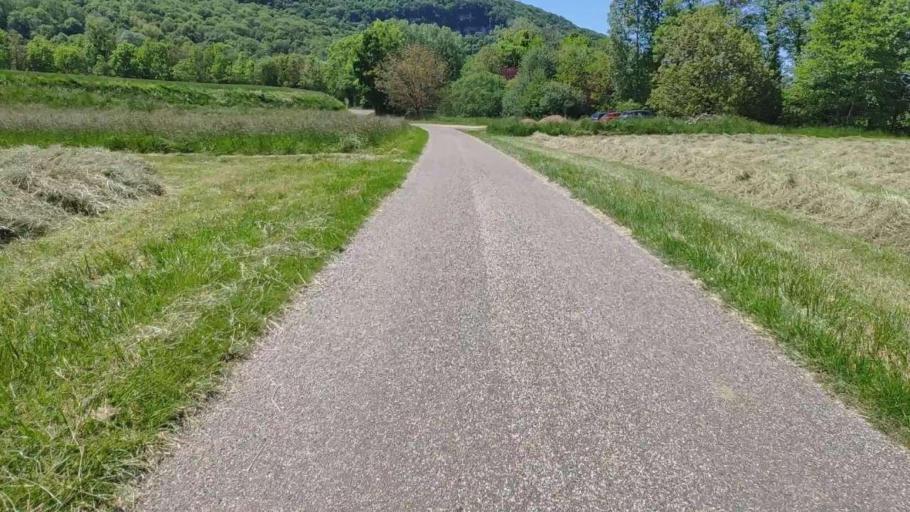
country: FR
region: Franche-Comte
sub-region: Departement du Jura
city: Perrigny
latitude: 46.7361
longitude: 5.6368
